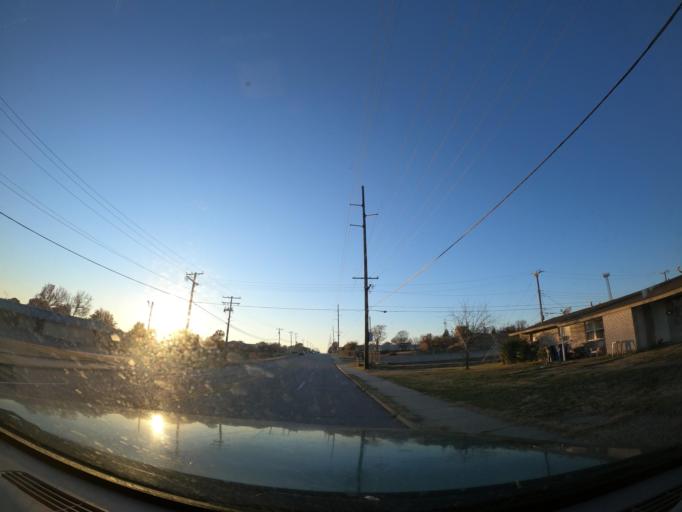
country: US
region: Oklahoma
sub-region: Tulsa County
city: Tulsa
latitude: 36.1408
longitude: -95.8959
